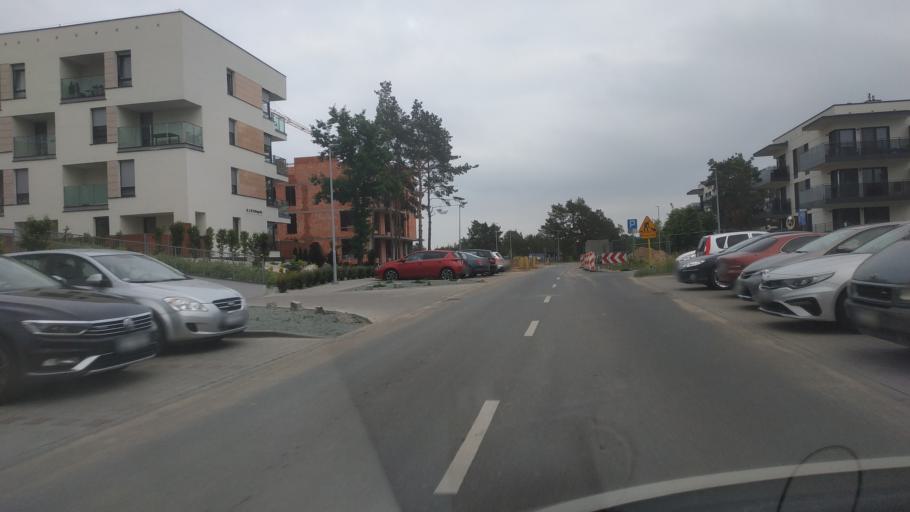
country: PL
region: Kujawsko-Pomorskie
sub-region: Torun
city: Torun
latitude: 53.0464
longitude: 18.6046
